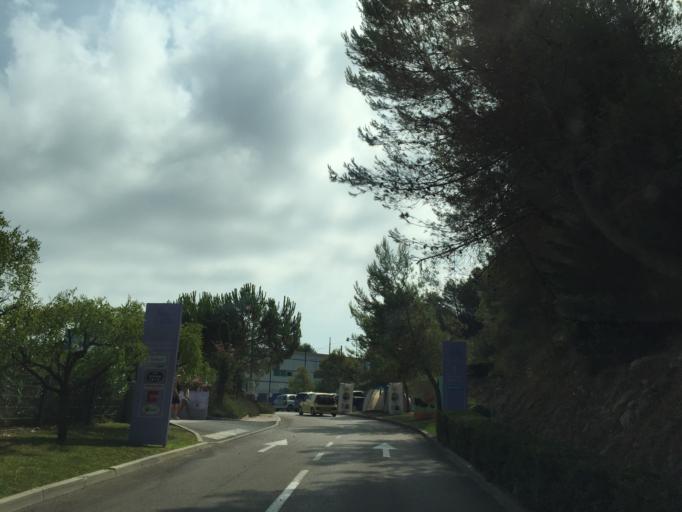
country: FR
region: Provence-Alpes-Cote d'Azur
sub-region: Departement des Alpes-Maritimes
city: Vallauris
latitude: 43.6004
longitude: 7.0764
